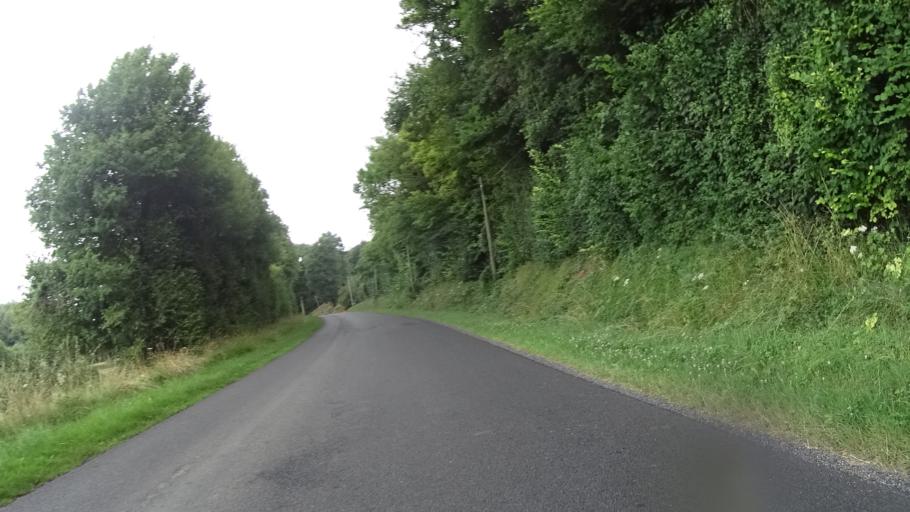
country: FR
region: Centre
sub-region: Departement du Loiret
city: Saint-Germain-des-Pres
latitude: 47.9258
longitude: 2.9016
